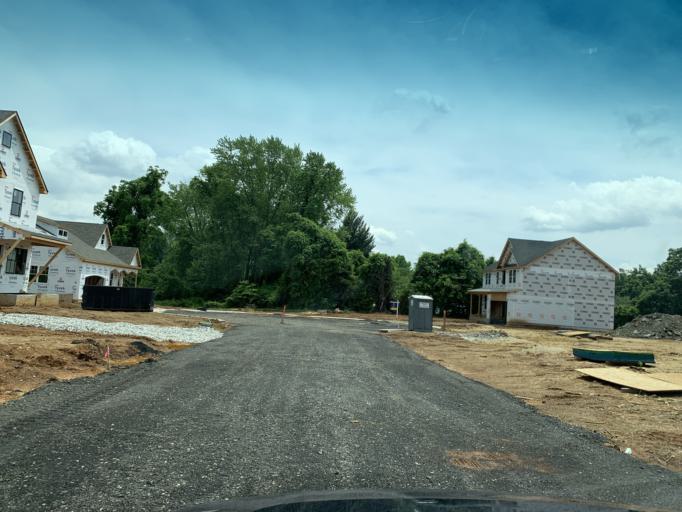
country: US
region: Maryland
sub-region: Harford County
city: North Bel Air
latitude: 39.5515
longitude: -76.3507
